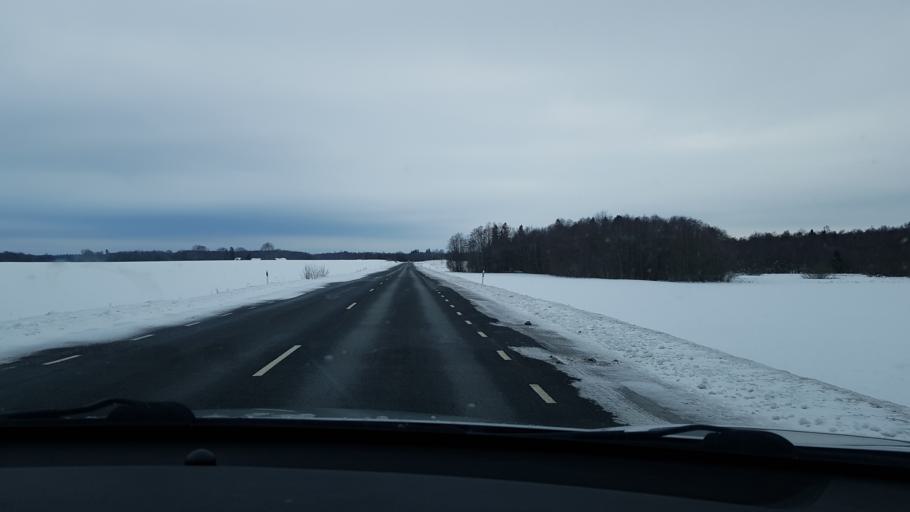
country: EE
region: Jaervamaa
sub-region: Jaerva-Jaani vald
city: Jarva-Jaani
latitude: 58.9018
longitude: 25.8059
